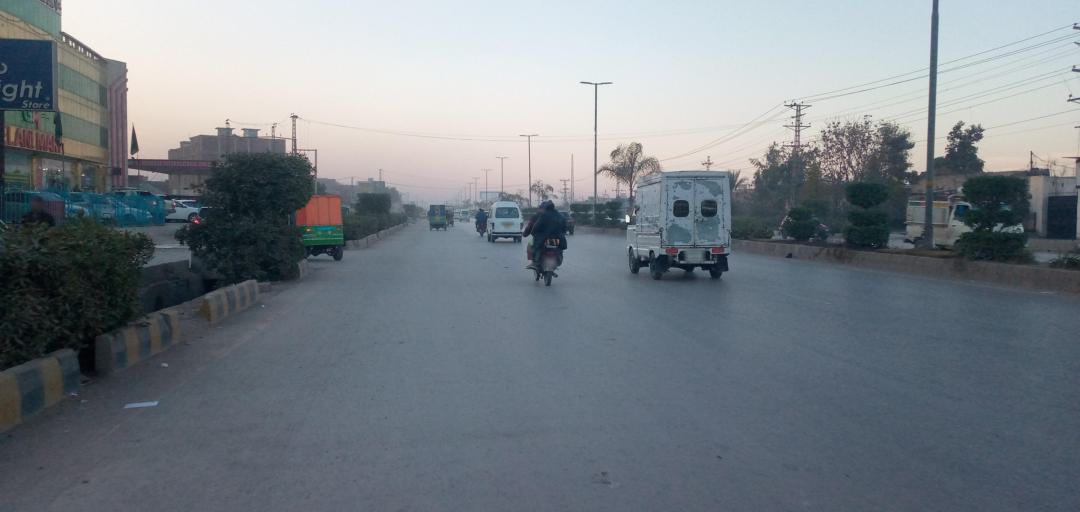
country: PK
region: Khyber Pakhtunkhwa
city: Peshawar
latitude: 34.0294
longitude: 71.6132
